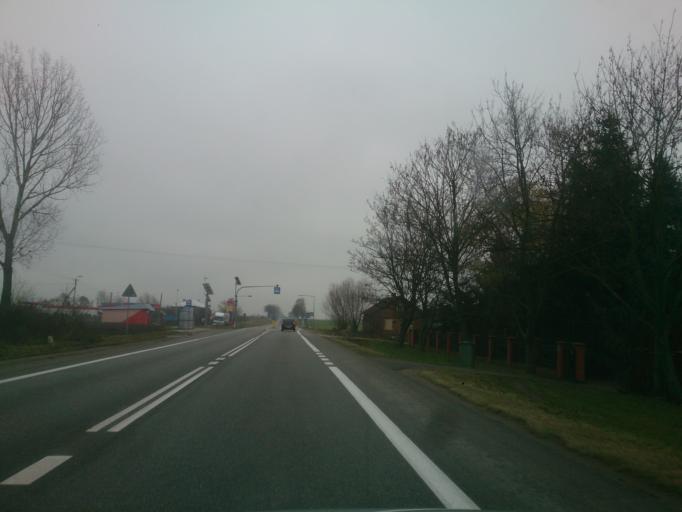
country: PL
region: Masovian Voivodeship
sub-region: Powiat plonski
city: Dzierzaznia
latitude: 52.6389
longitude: 20.1405
